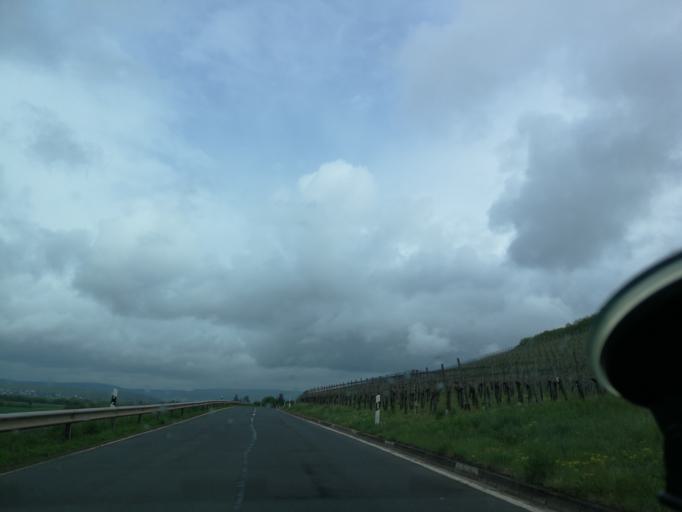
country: DE
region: Rheinland-Pfalz
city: Osann-Monzel
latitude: 49.9310
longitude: 6.9453
